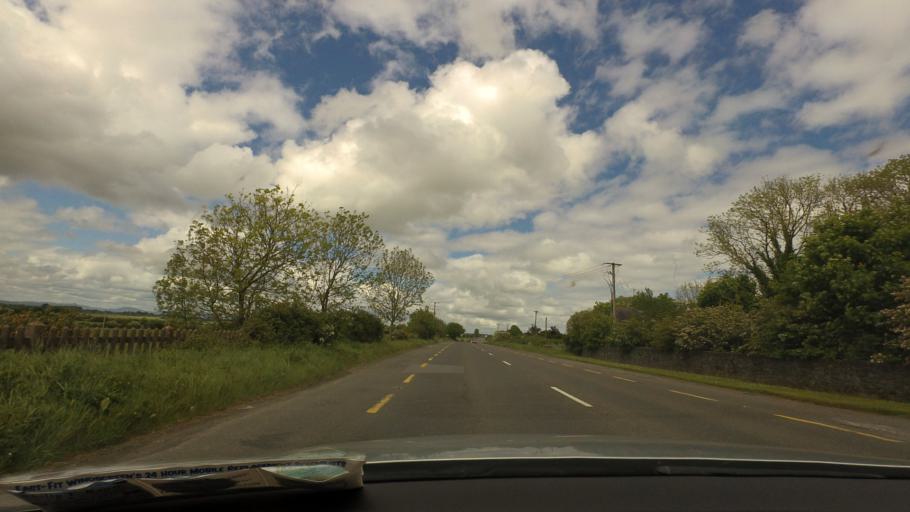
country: IE
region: Munster
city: Cashel
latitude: 52.5371
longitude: -7.8735
